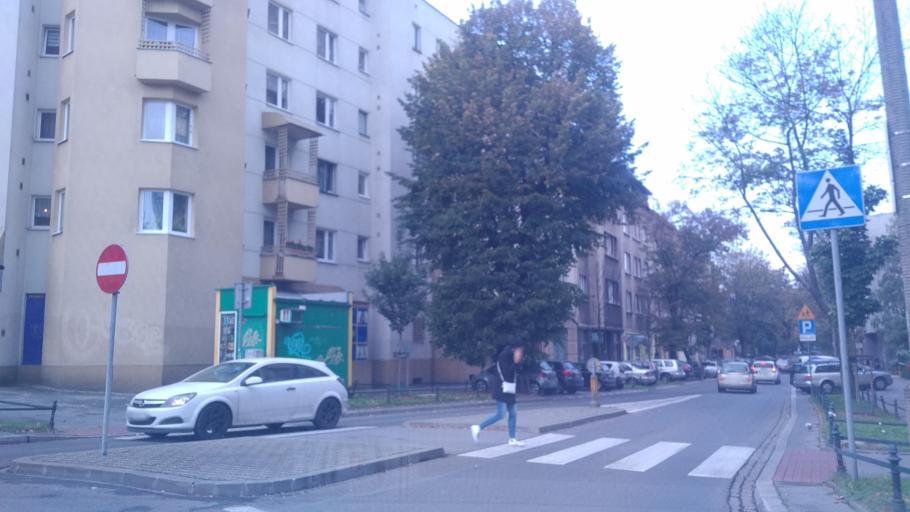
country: PL
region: Lesser Poland Voivodeship
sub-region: Krakow
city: Krakow
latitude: 50.0744
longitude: 19.9289
